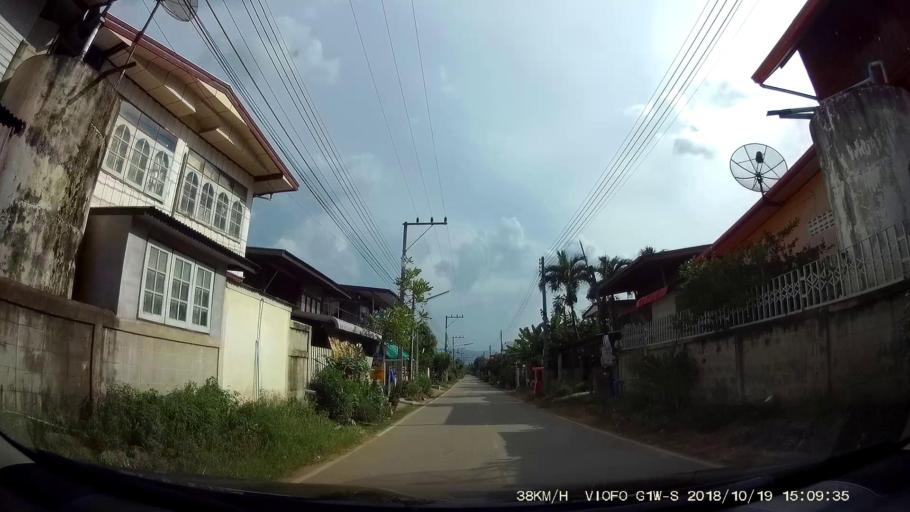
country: TH
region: Chaiyaphum
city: Phu Khiao
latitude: 16.4099
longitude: 102.1033
